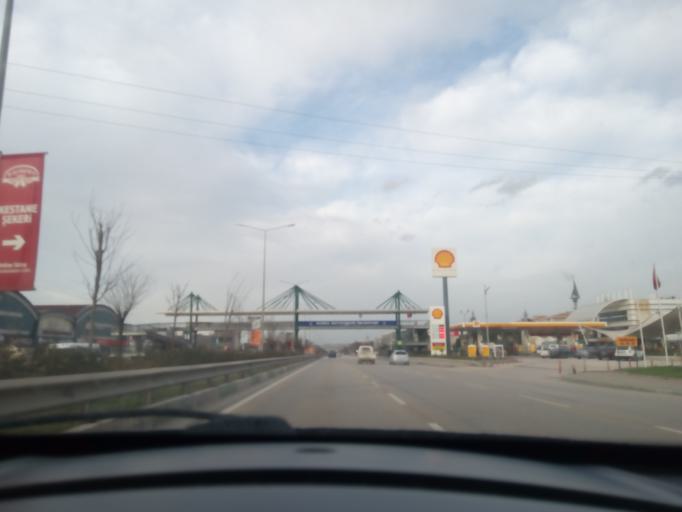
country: TR
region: Bursa
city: Cali
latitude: 40.2125
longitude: 28.9312
